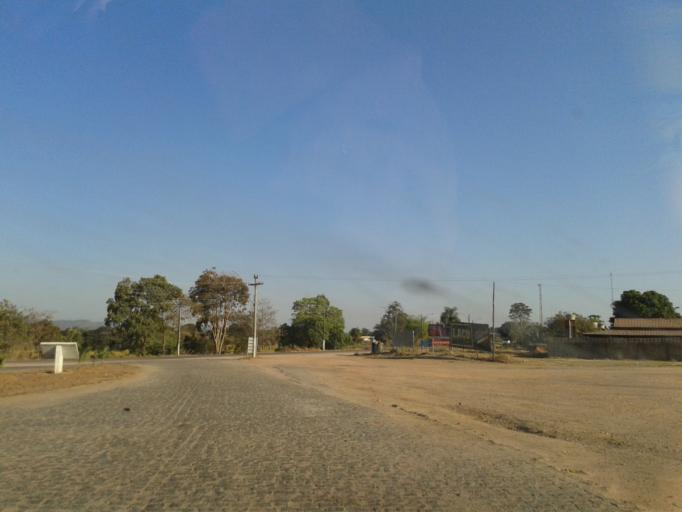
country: BR
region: Goias
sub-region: Itapuranga
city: Itapuranga
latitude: -15.4535
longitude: -50.3596
